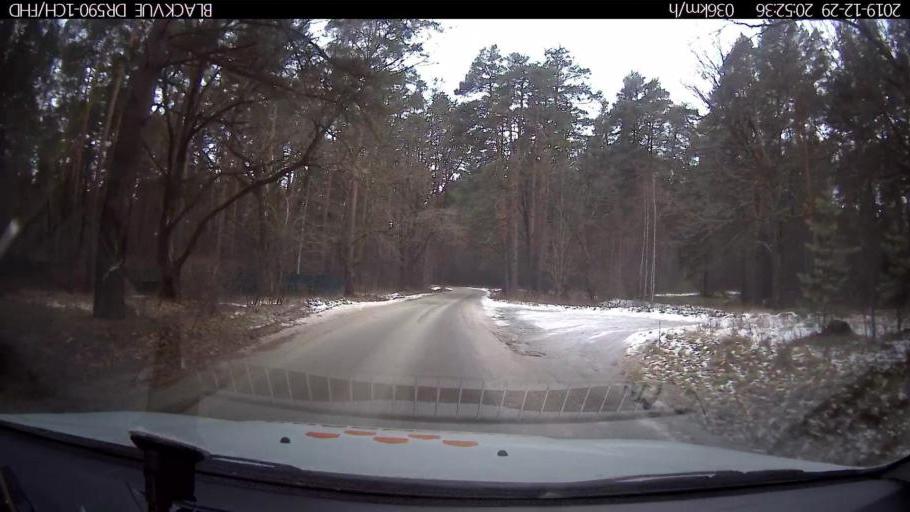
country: RU
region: Nizjnij Novgorod
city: Afonino
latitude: 56.1757
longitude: 43.9920
